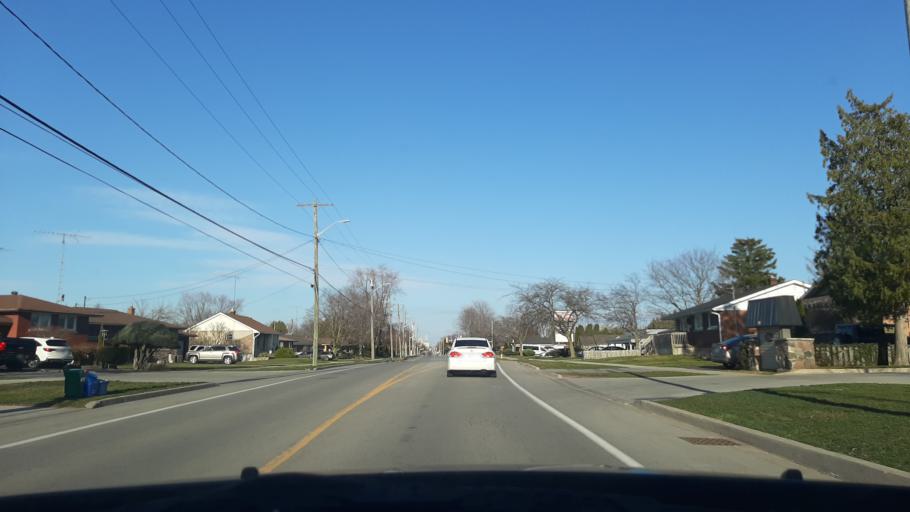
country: CA
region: Ontario
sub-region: Regional Municipality of Niagara
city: St. Catharines
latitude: 43.2128
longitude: -79.2251
